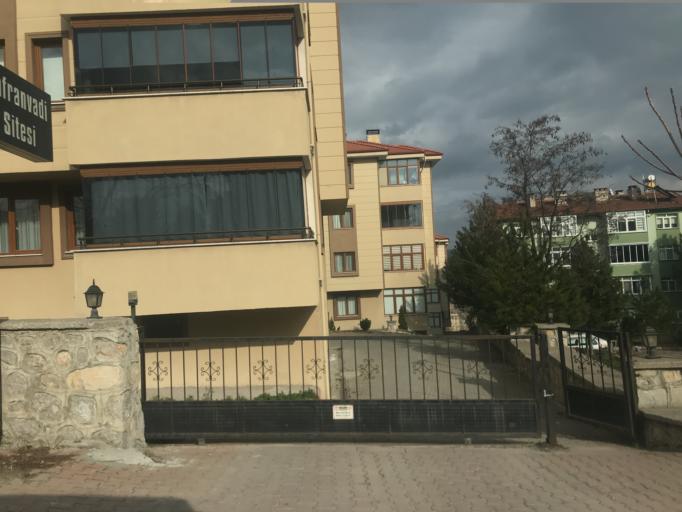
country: TR
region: Karabuk
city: Safranbolu
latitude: 41.2552
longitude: 32.6821
